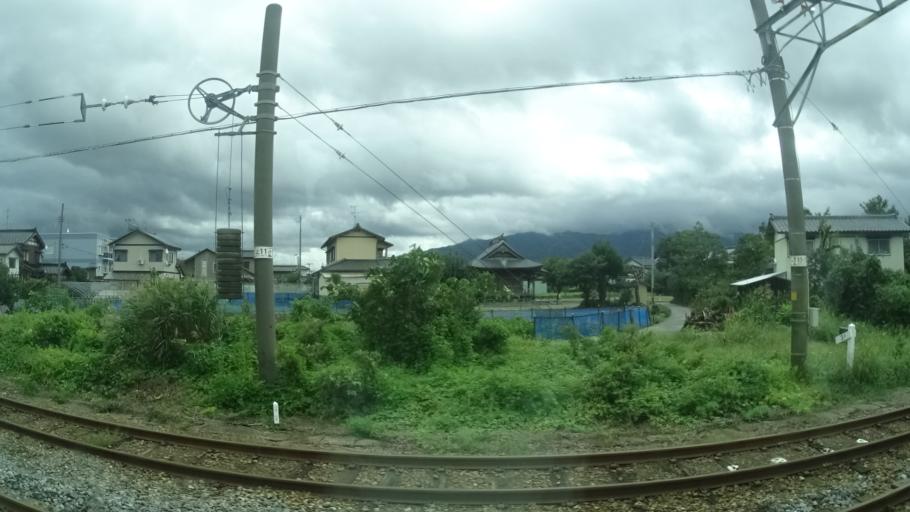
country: JP
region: Niigata
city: Murakami
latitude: 38.1179
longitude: 139.4447
